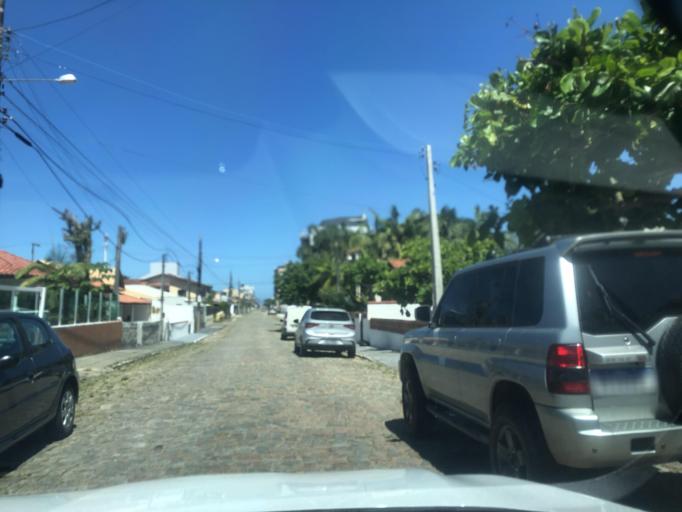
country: BR
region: Santa Catarina
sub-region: Sao Francisco Do Sul
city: Sao Francisco do Sul
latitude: -26.2284
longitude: -48.5090
